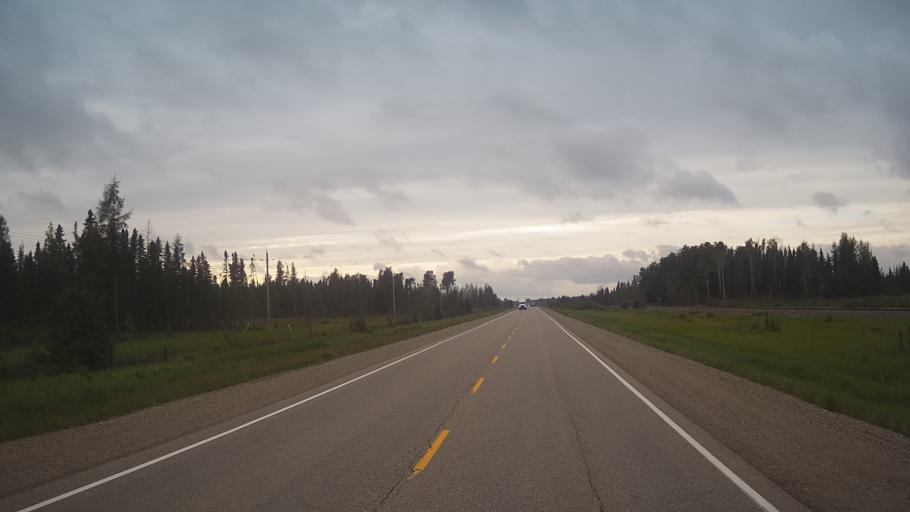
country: CA
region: Ontario
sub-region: Thunder Bay District
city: Thunder Bay
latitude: 48.8663
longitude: -89.9703
